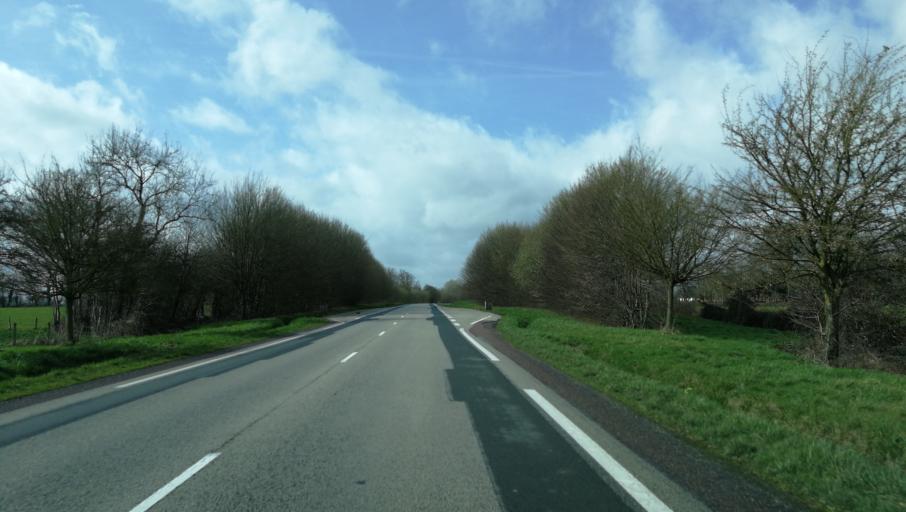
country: FR
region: Haute-Normandie
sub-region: Departement de l'Eure
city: Epaignes
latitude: 49.2903
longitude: 0.3963
